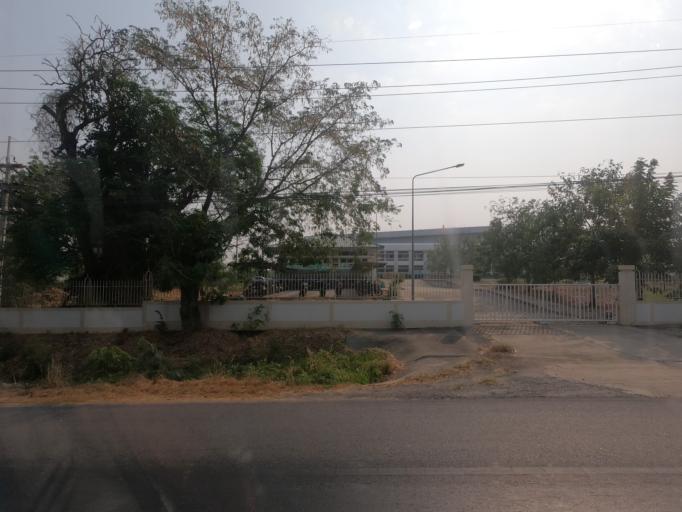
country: TH
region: Khon Kaen
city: Ban Haet
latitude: 16.1748
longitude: 102.7559
